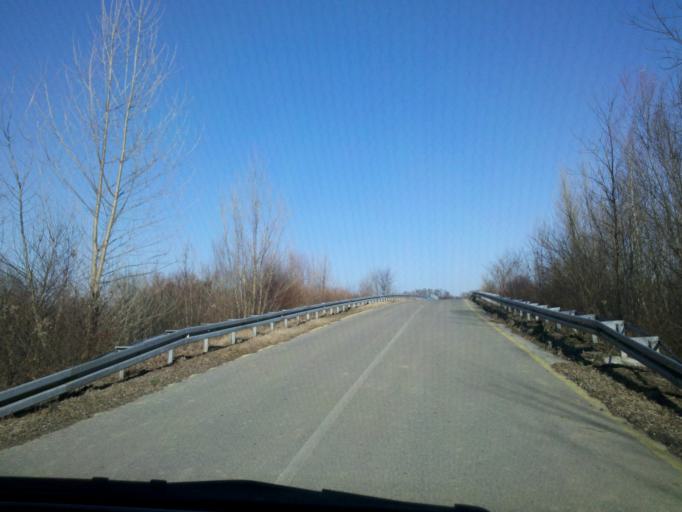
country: HR
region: Medimurska
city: Gorican
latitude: 46.4062
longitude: 16.6731
